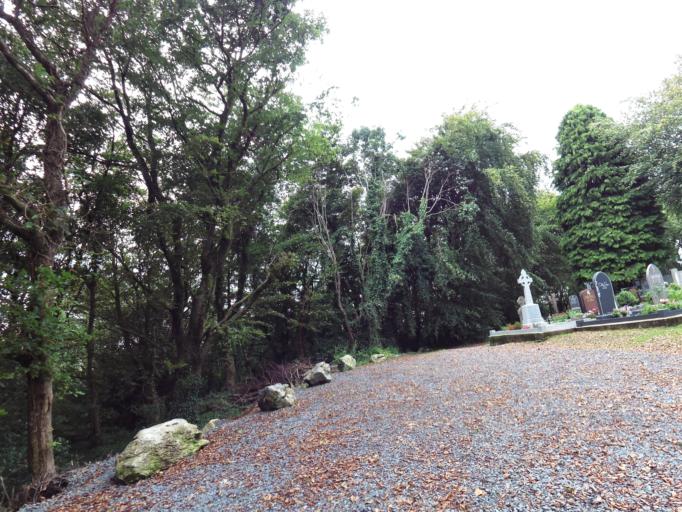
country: IE
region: Connaught
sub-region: County Galway
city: Gaillimh
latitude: 53.2999
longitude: -9.0775
